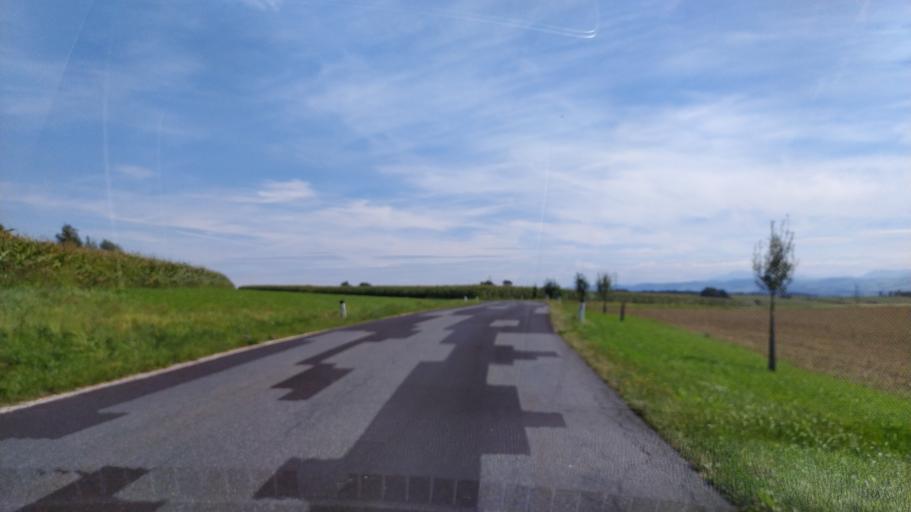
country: AT
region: Lower Austria
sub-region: Politischer Bezirk Amstetten
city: Wolfsbach
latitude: 48.1156
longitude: 14.7154
